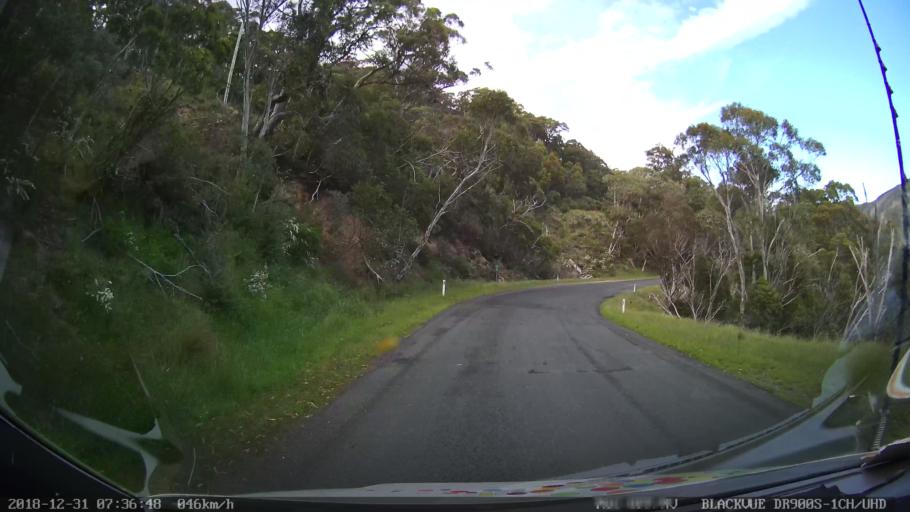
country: AU
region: New South Wales
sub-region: Snowy River
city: Jindabyne
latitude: -36.3431
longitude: 148.4411
